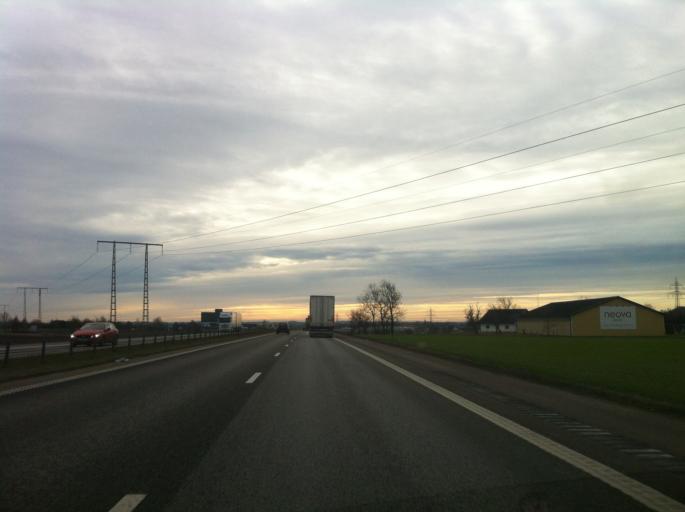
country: SE
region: Skane
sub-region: Astorps Kommun
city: Astorp
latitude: 56.1389
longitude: 12.9269
